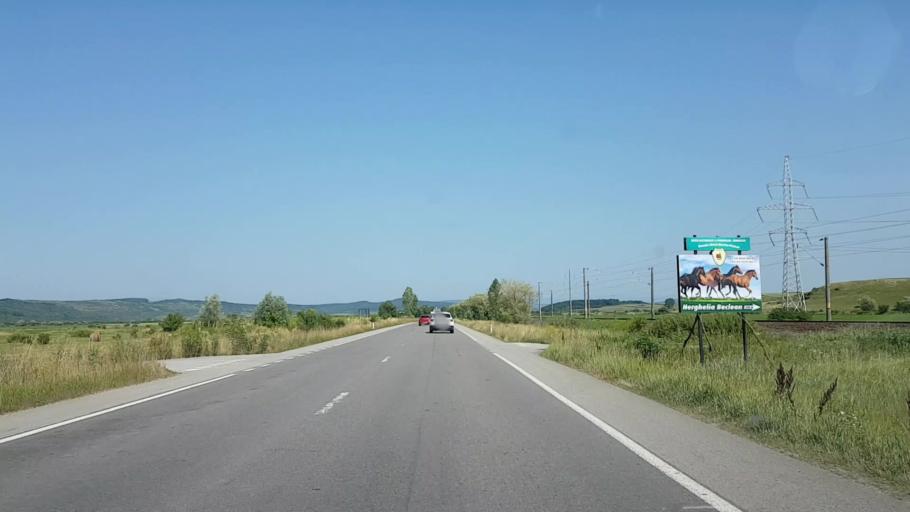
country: RO
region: Bistrita-Nasaud
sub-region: Comuna Sintereag
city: Cociu
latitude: 47.1837
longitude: 24.2168
